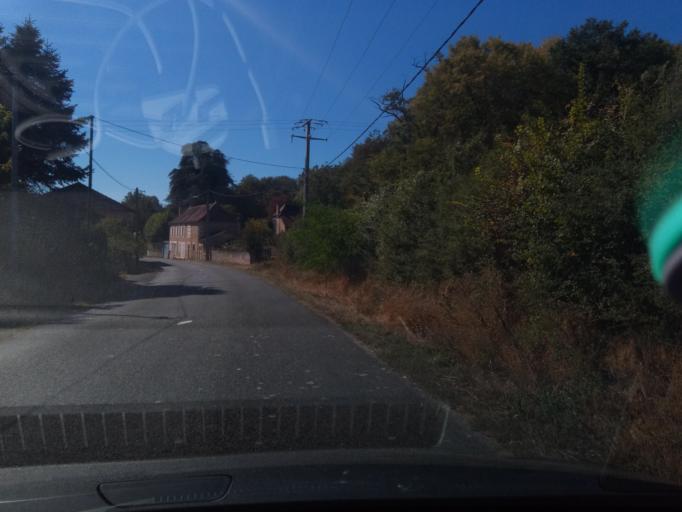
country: FR
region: Poitou-Charentes
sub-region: Departement de la Vienne
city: Saulge
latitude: 46.4015
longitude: 0.8737
